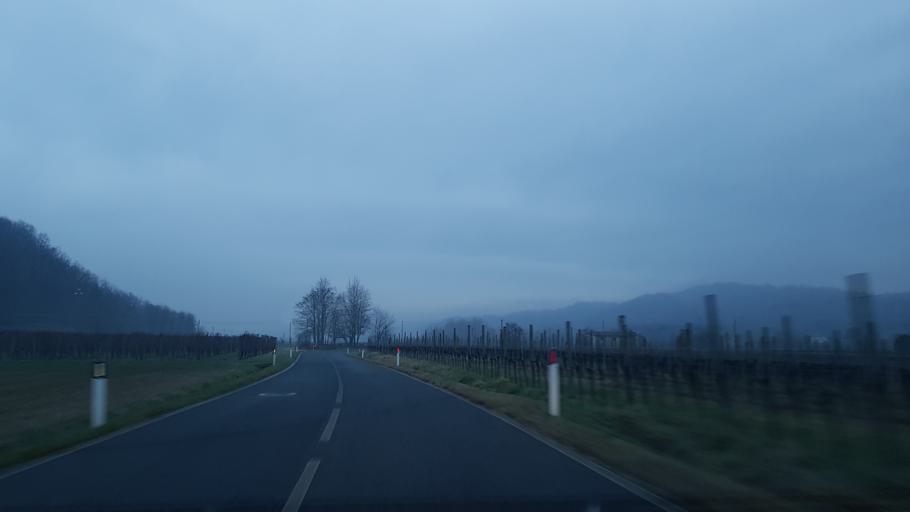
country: IT
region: Friuli Venezia Giulia
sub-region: Provincia di Udine
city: Prepotto
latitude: 46.0426
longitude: 13.4884
